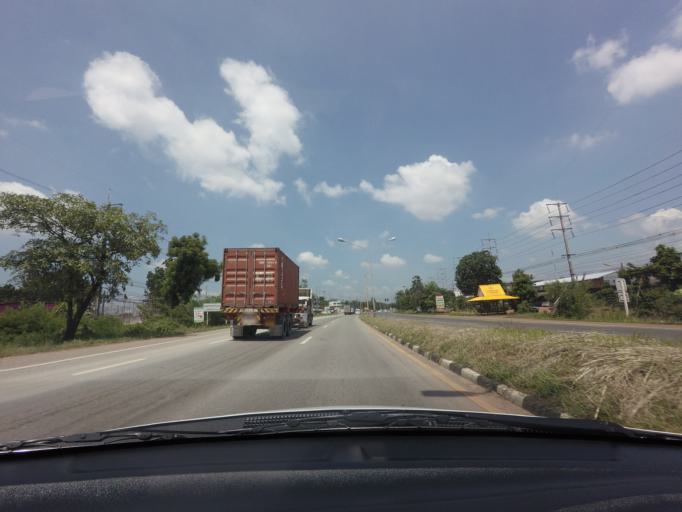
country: TH
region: Prachin Buri
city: Si Maha Phot
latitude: 13.8603
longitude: 101.5545
